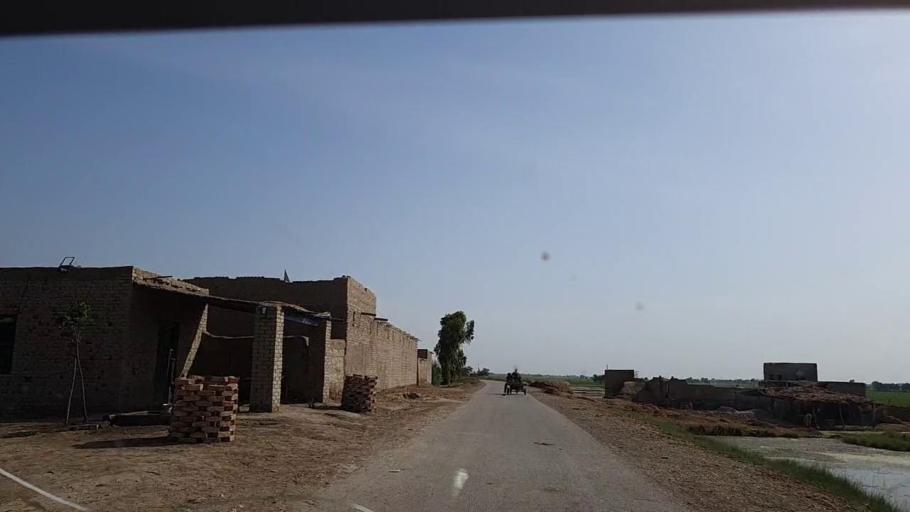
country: PK
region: Sindh
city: Khairpur Nathan Shah
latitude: 27.0010
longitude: 67.6681
